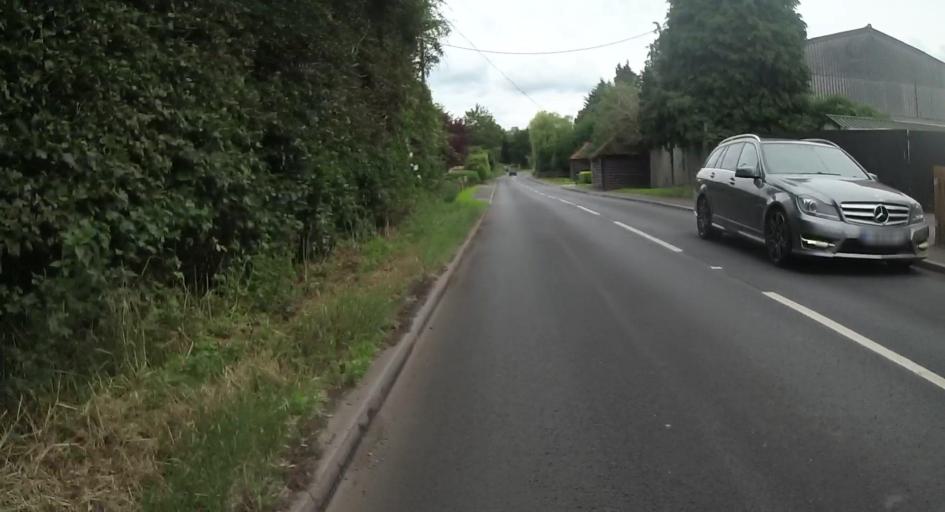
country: GB
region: England
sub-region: Wokingham
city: Barkham
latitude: 51.3937
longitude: -0.8786
